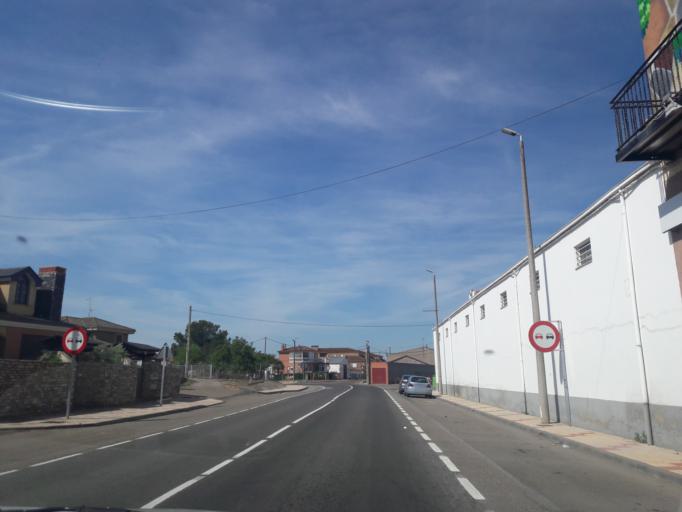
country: ES
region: Castille and Leon
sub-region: Provincia de Salamanca
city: Babilafuente
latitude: 40.9737
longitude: -5.4264
